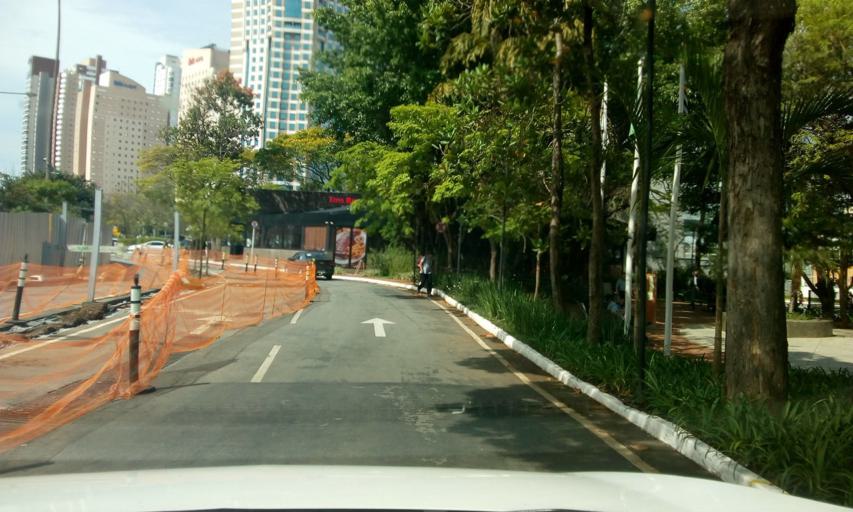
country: BR
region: Sao Paulo
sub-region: Taboao Da Serra
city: Taboao da Serra
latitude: -23.6243
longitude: -46.6983
